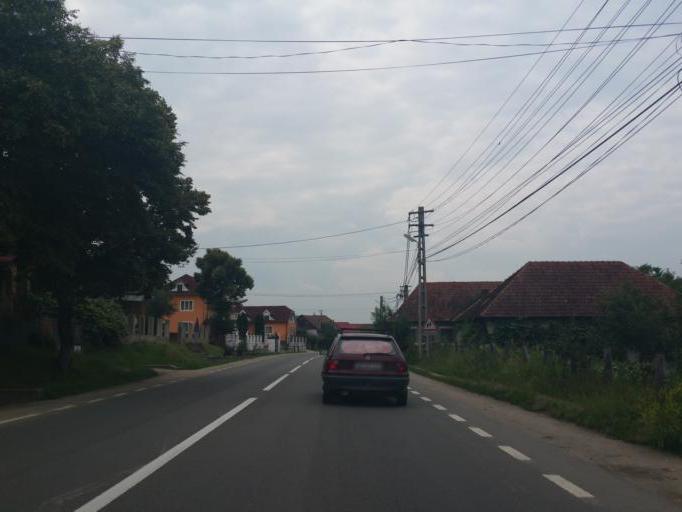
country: RO
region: Salaj
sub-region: Comuna Hida
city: Hida
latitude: 47.0400
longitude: 23.2615
